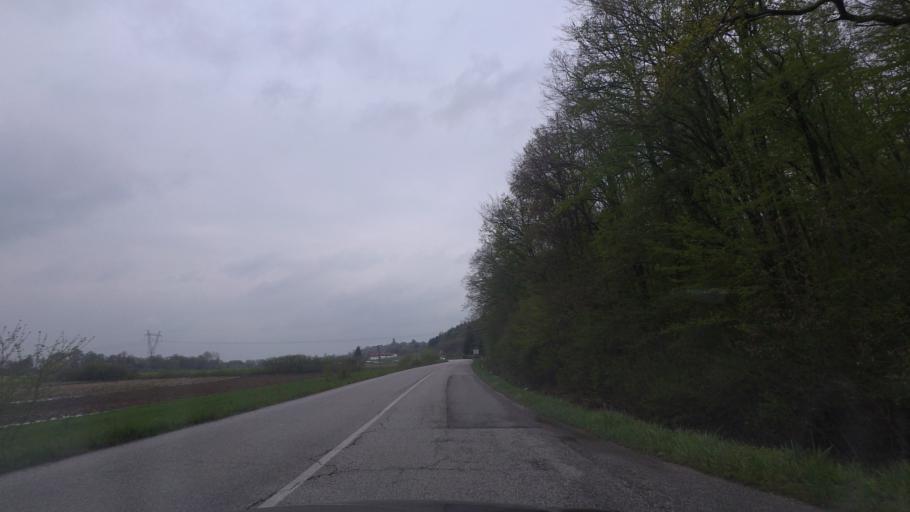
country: HR
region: Karlovacka
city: Ozalj
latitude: 45.6244
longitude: 15.5568
